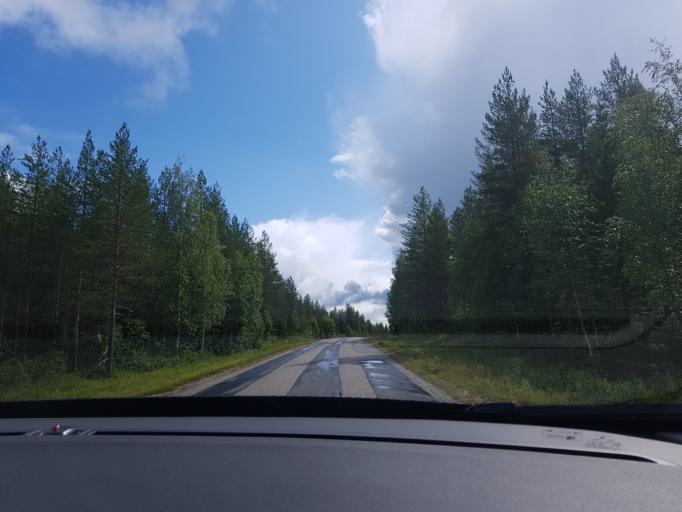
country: FI
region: Kainuu
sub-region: Kehys-Kainuu
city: Kuhmo
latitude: 64.4598
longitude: 29.6352
